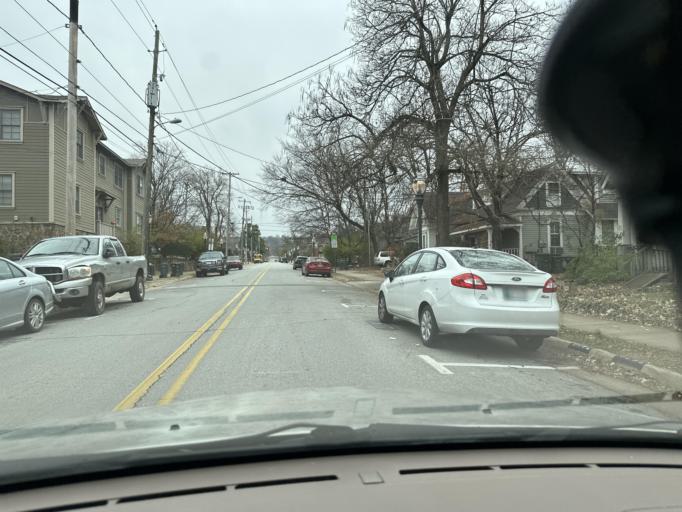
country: US
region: Arkansas
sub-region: Washington County
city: Fayetteville
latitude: 36.0647
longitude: -94.1638
